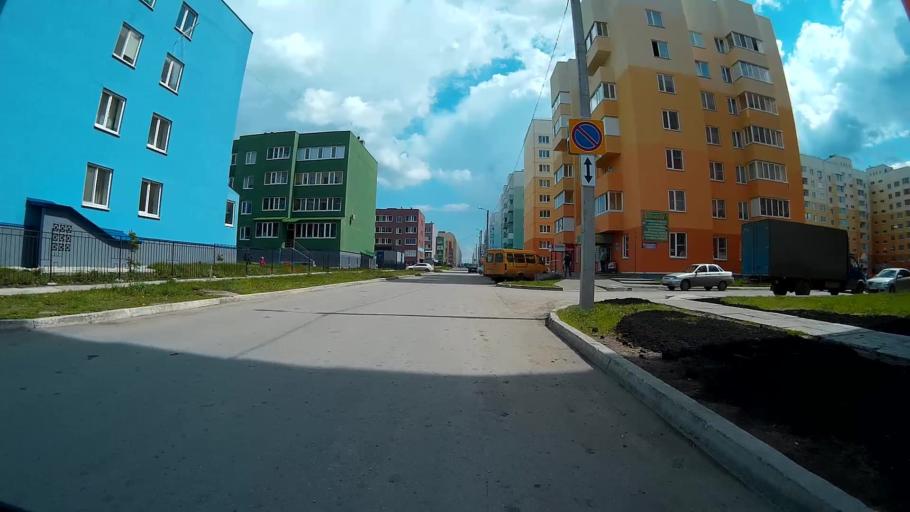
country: RU
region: Ulyanovsk
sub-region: Ulyanovskiy Rayon
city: Ulyanovsk
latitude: 54.3483
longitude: 48.3364
